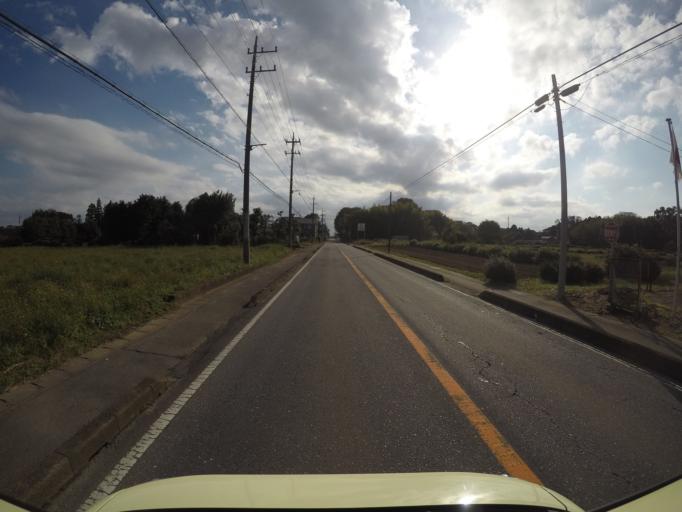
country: JP
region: Ibaraki
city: Iwai
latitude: 36.0013
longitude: 139.9049
